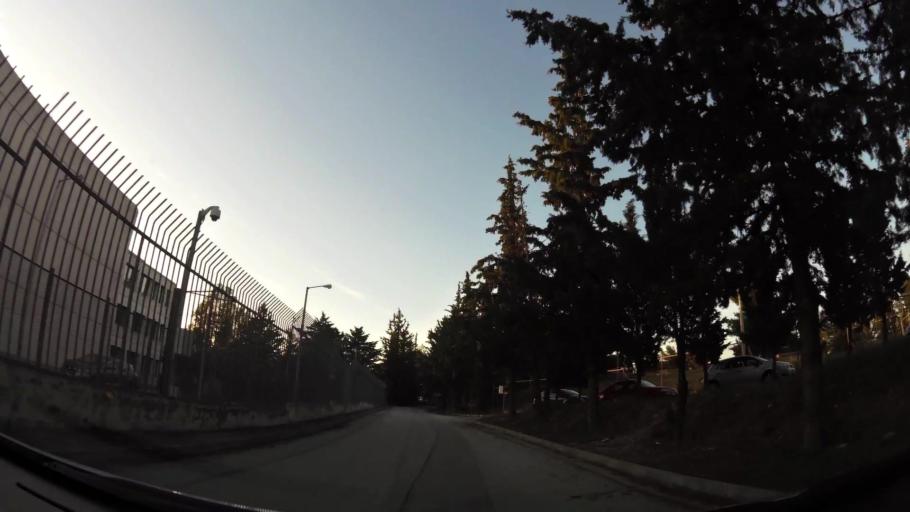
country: GR
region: Attica
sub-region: Nomarchia Anatolikis Attikis
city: Kryoneri
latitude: 38.1298
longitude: 23.8347
